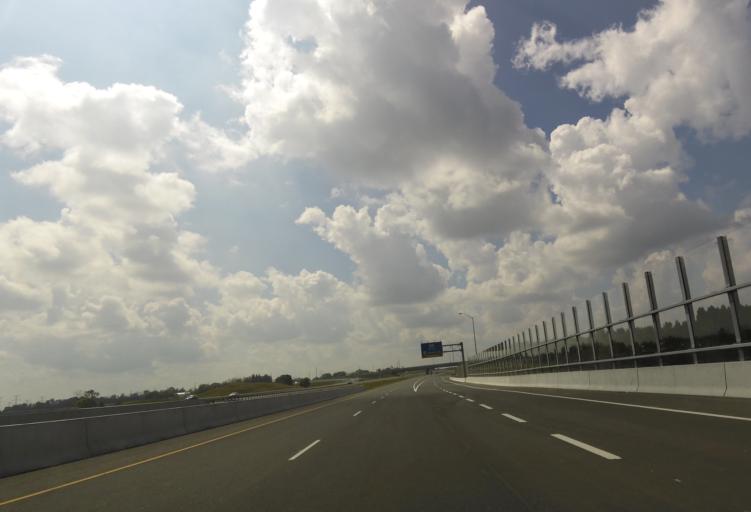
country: CA
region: Ontario
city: Oshawa
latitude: 43.9486
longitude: -78.9526
